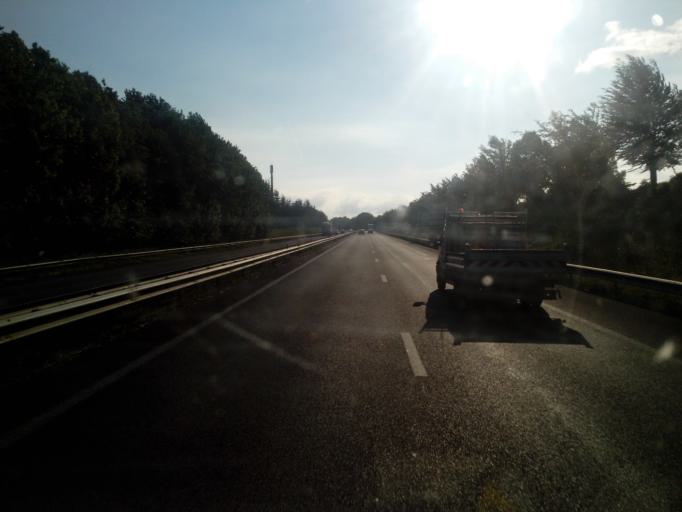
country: FR
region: Lower Normandy
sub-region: Departement du Calvados
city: Grainville-sur-Odon
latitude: 49.1438
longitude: -0.5263
